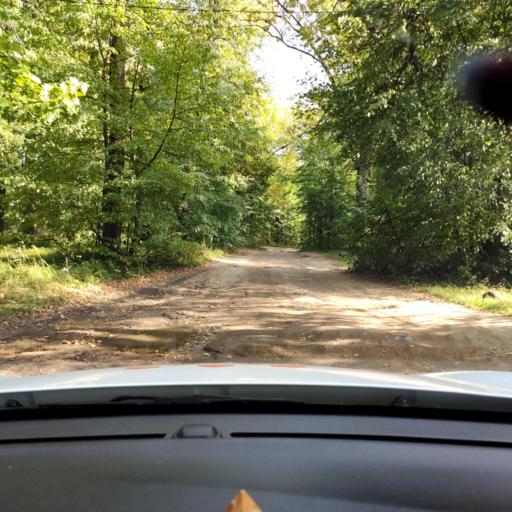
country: RU
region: Tatarstan
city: Staroye Arakchino
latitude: 55.8068
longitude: 49.0153
